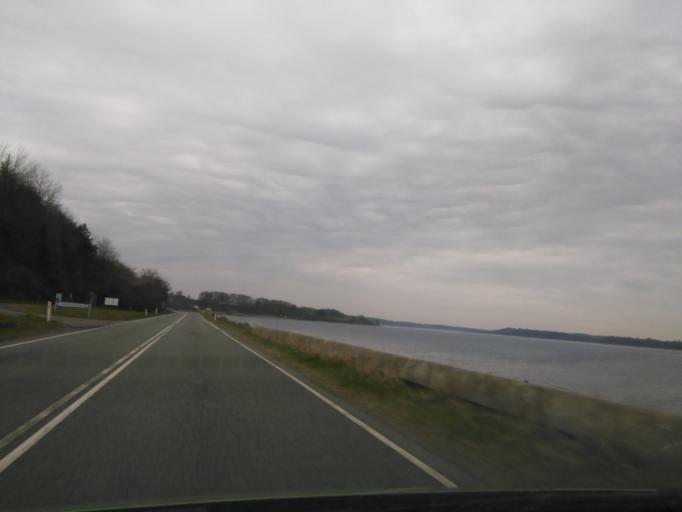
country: DK
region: North Denmark
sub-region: Mariagerfjord Kommune
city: Mariager
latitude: 56.6698
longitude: 10.0076
